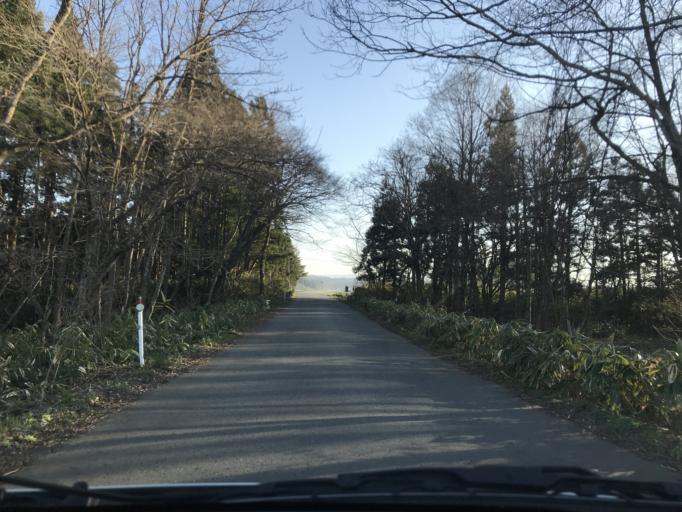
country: JP
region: Iwate
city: Kitakami
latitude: 39.2218
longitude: 141.0416
